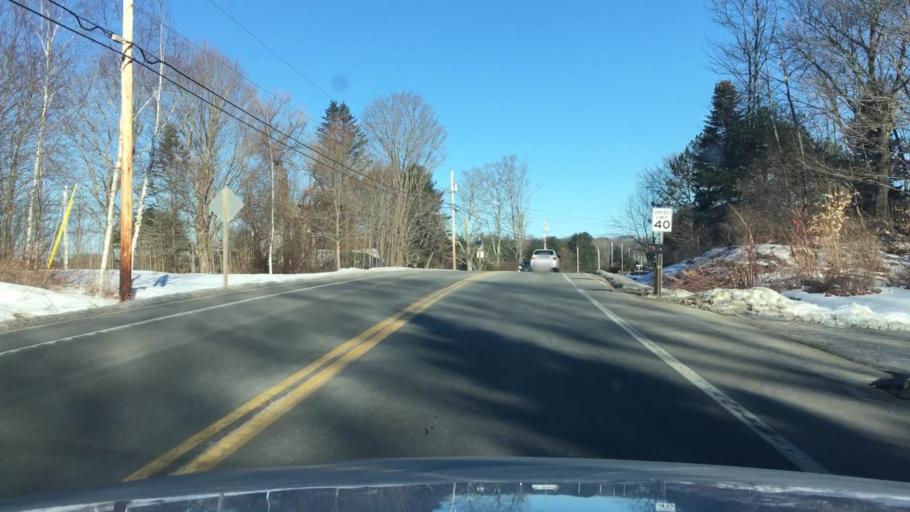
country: US
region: Maine
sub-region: Cumberland County
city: Freeport
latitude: 43.9011
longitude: -70.1160
